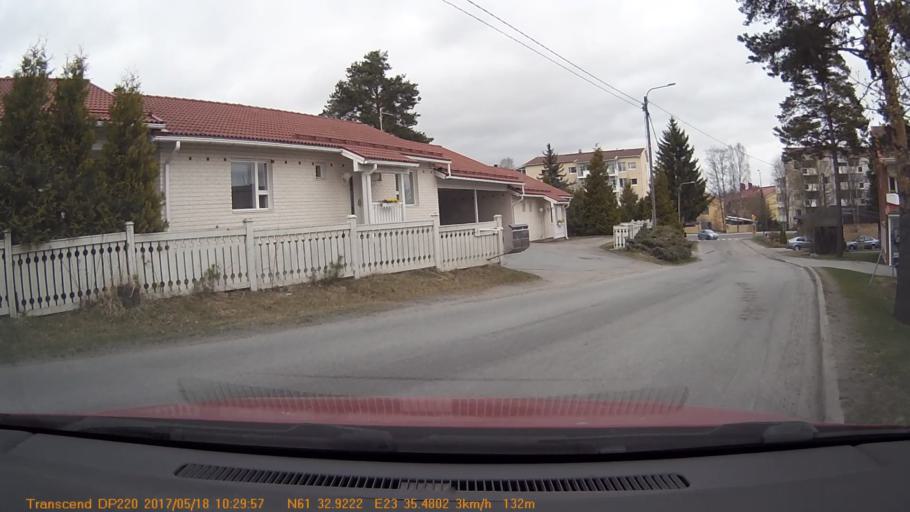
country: FI
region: Pirkanmaa
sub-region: Tampere
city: Yloejaervi
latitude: 61.5486
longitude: 23.5913
